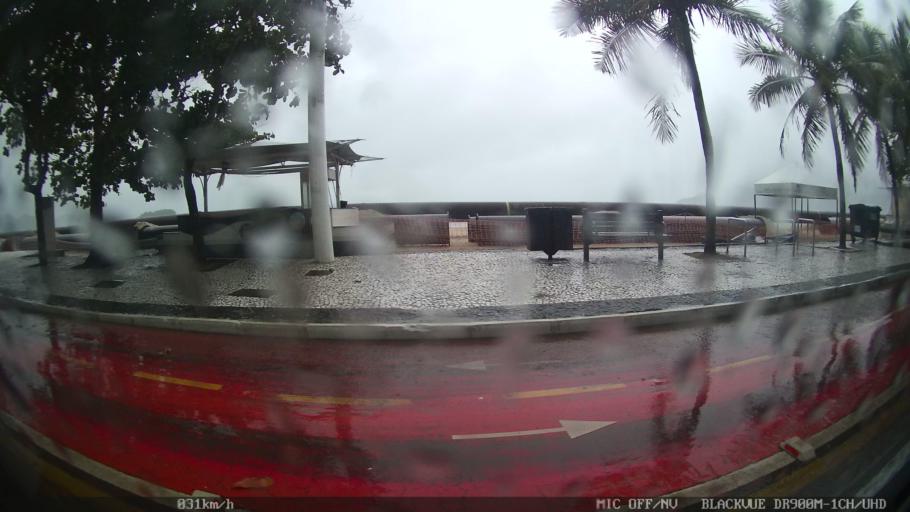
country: BR
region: Santa Catarina
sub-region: Balneario Camboriu
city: Balneario Camboriu
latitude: -26.9955
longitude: -48.6264
